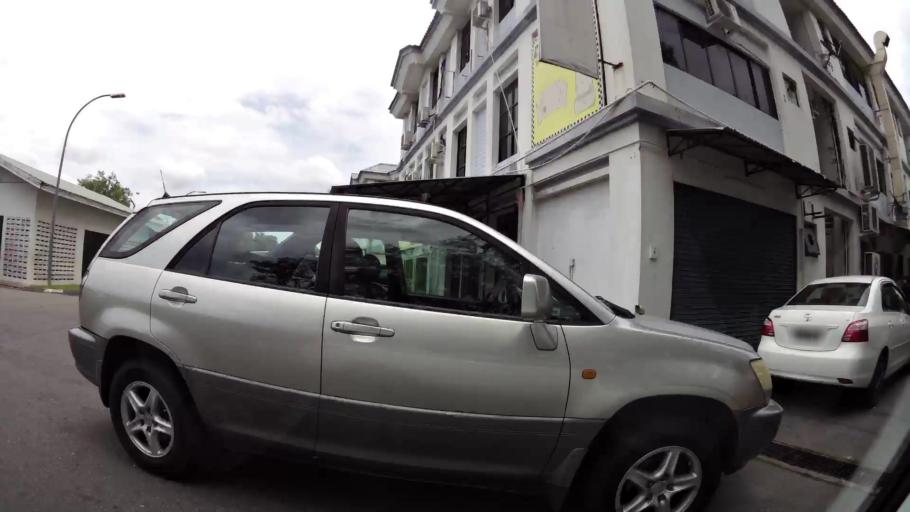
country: BN
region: Brunei and Muara
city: Bandar Seri Begawan
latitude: 4.9177
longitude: 114.9128
